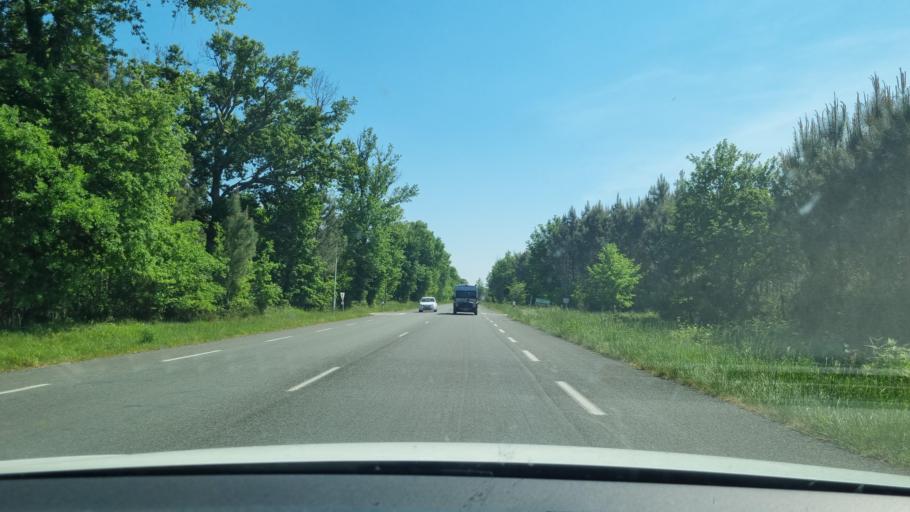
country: FR
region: Aquitaine
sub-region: Departement de la Gironde
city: Prechac
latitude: 44.2492
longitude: -0.2611
